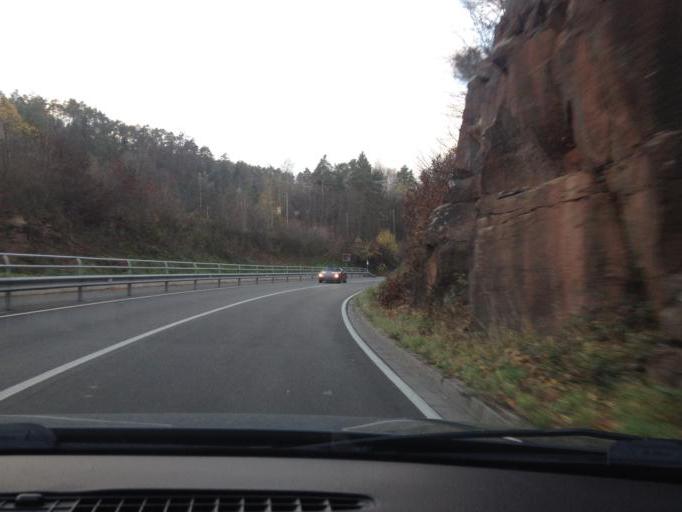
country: DE
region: Rheinland-Pfalz
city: Weidenthal
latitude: 49.4053
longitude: 8.0139
